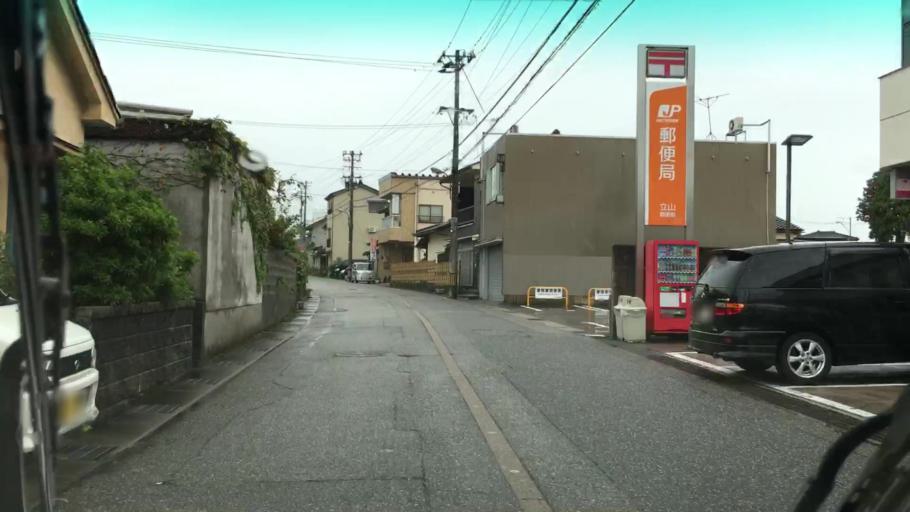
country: JP
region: Toyama
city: Kamiichi
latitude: 36.6633
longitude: 137.3161
